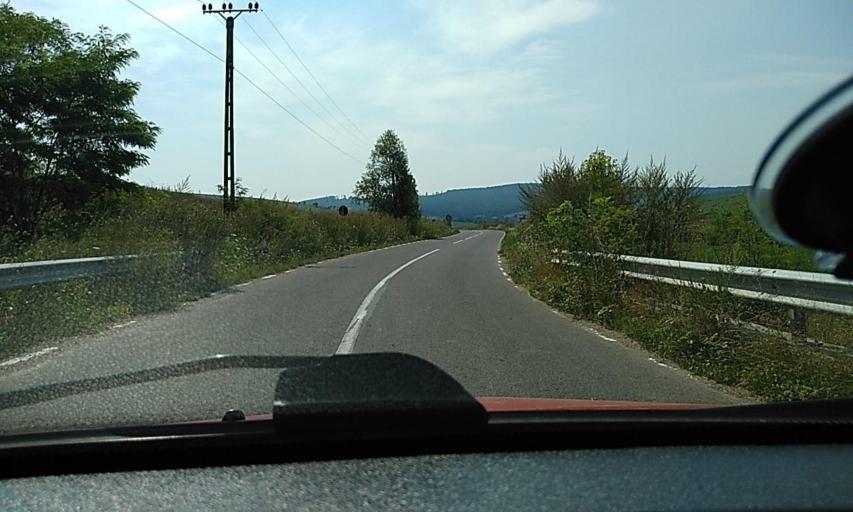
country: RO
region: Brasov
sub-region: Oras Rupea
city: Fiser
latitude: 46.0279
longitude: 25.1448
